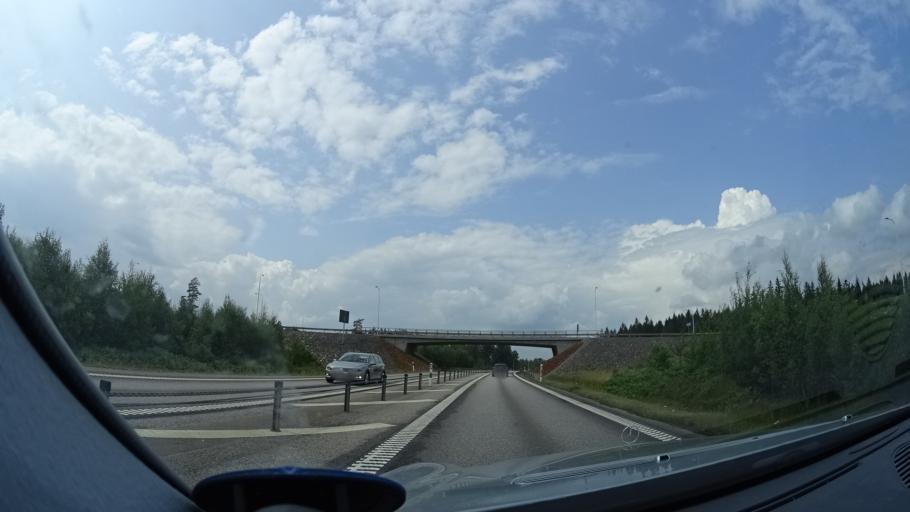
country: SE
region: Kalmar
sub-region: Nybro Kommun
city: Nybro
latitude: 56.7278
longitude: 15.8874
